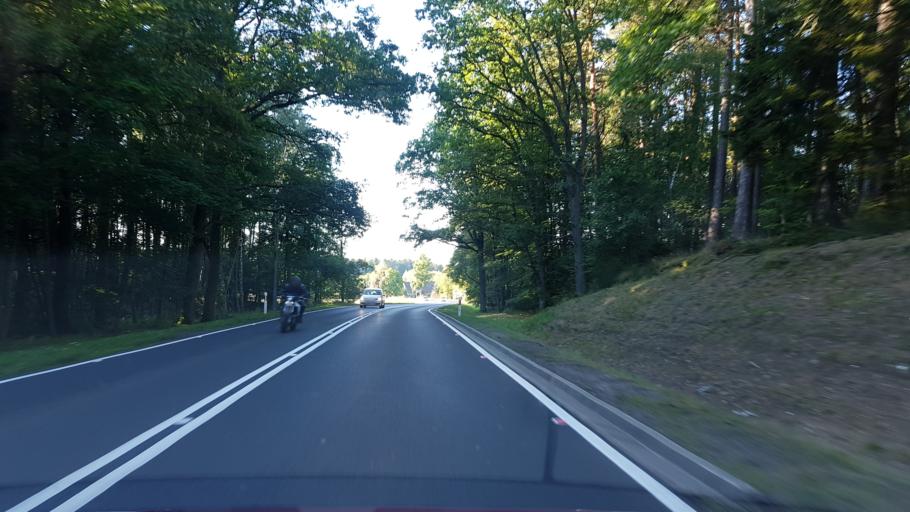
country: PL
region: West Pomeranian Voivodeship
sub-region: Powiat koszalinski
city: Bobolice
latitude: 53.9982
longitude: 16.5259
